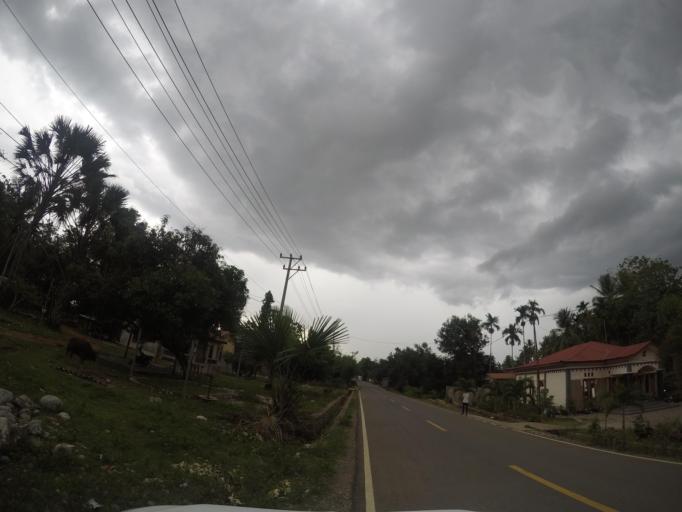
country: TL
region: Bobonaro
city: Maliana
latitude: -8.9664
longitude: 125.2172
